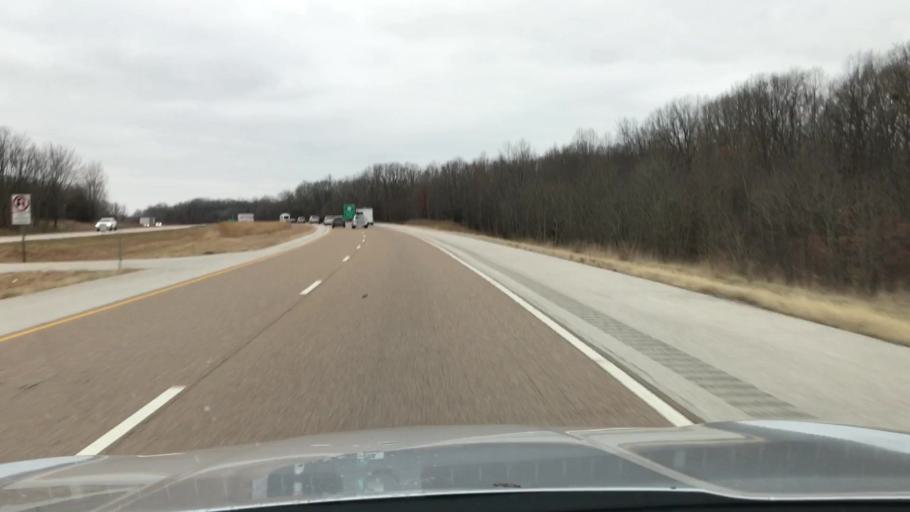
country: US
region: Illinois
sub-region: Macoupin County
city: Mount Olive
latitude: 39.0843
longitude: -89.7532
